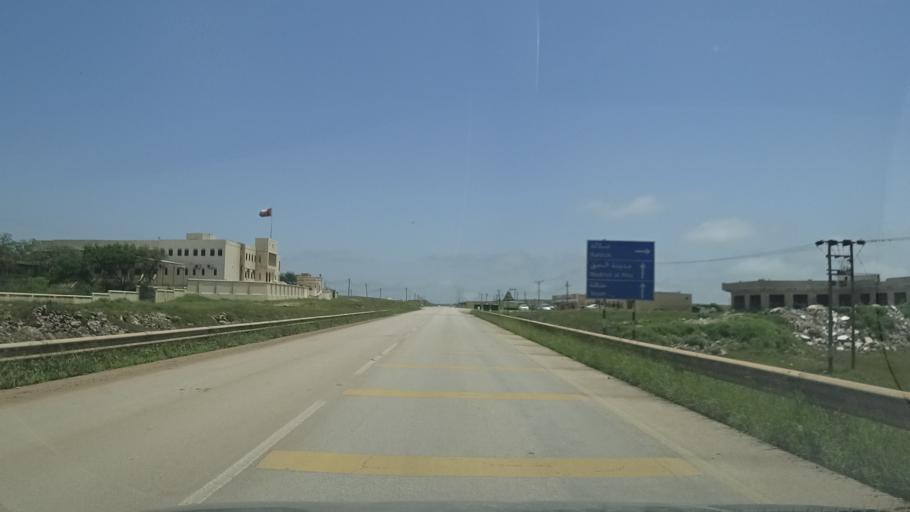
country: OM
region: Zufar
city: Salalah
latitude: 17.2427
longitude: 54.2828
